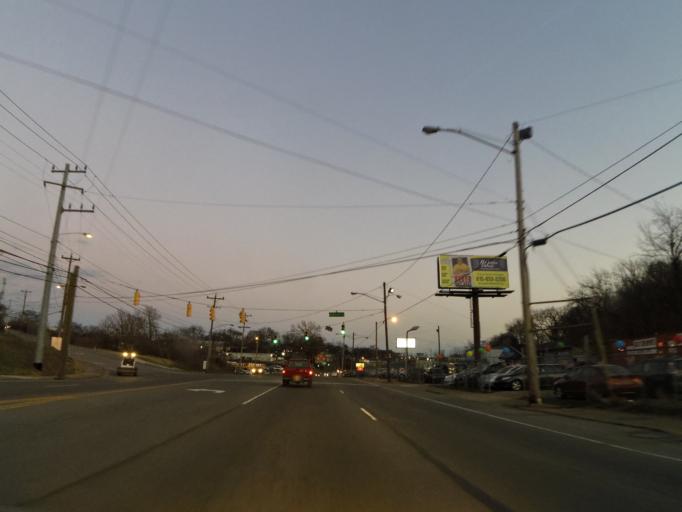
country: US
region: Tennessee
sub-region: Davidson County
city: Nashville
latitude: 36.1314
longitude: -86.7564
